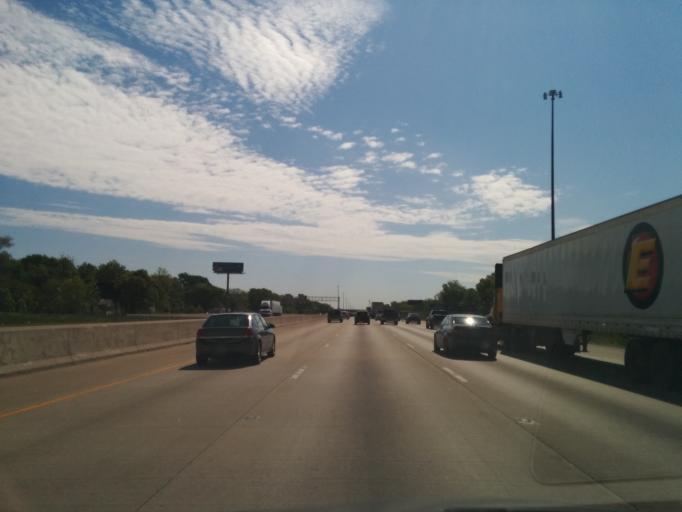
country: US
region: Indiana
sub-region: Lake County
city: Griffith
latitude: 41.5698
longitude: -87.4023
